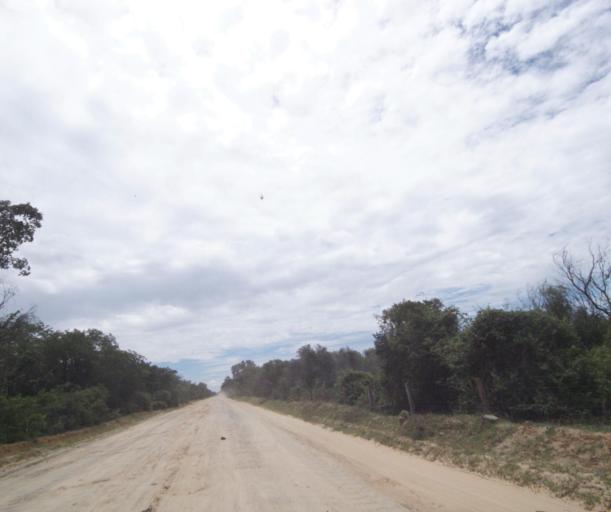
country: BR
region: Bahia
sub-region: Carinhanha
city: Carinhanha
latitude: -14.2144
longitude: -43.8934
